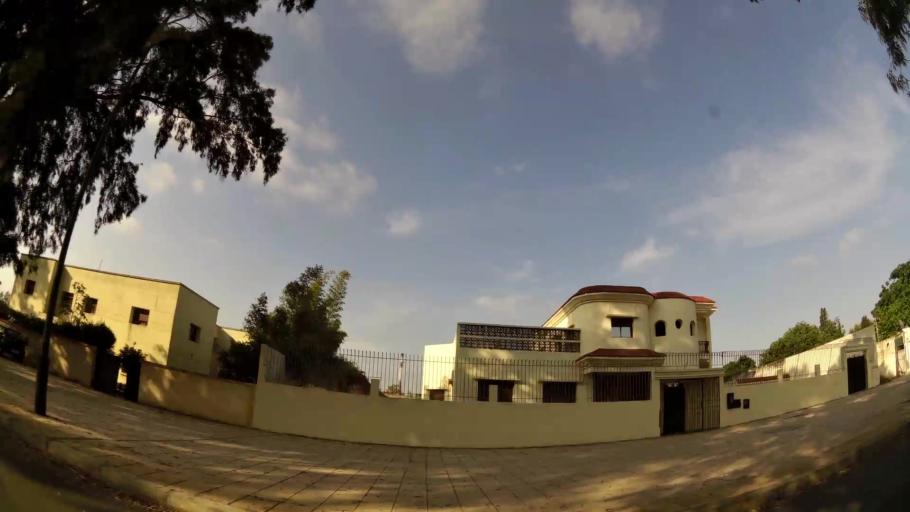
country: MA
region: Rabat-Sale-Zemmour-Zaer
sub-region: Rabat
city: Rabat
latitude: 33.9383
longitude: -6.8193
